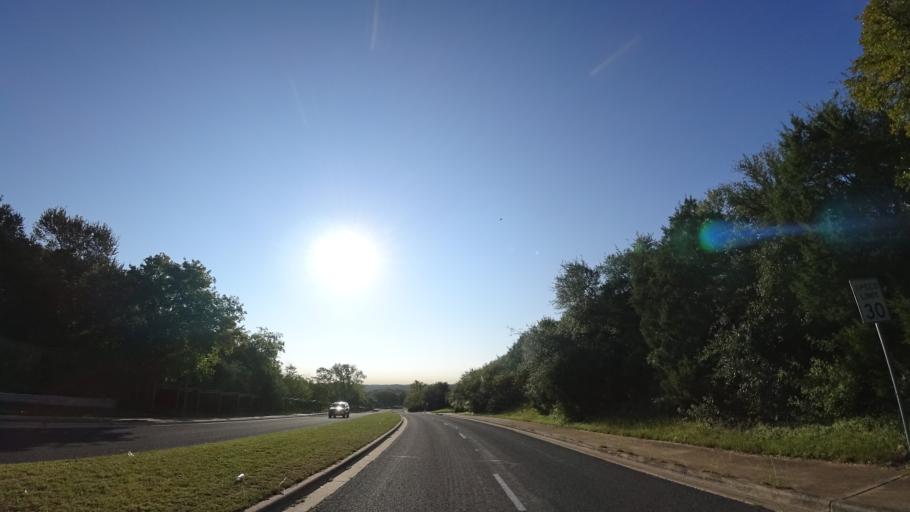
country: US
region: Texas
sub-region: Travis County
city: Rollingwood
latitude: 30.2602
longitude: -97.8055
